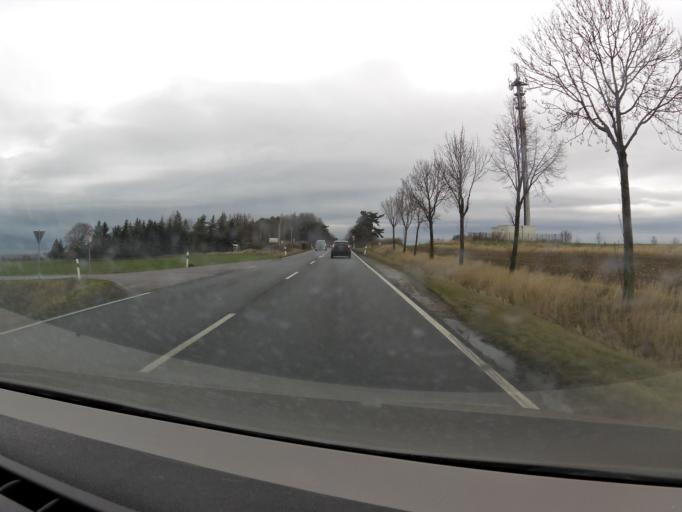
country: DE
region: Saxony-Anhalt
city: Aschersleben
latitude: 51.7358
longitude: 11.4545
